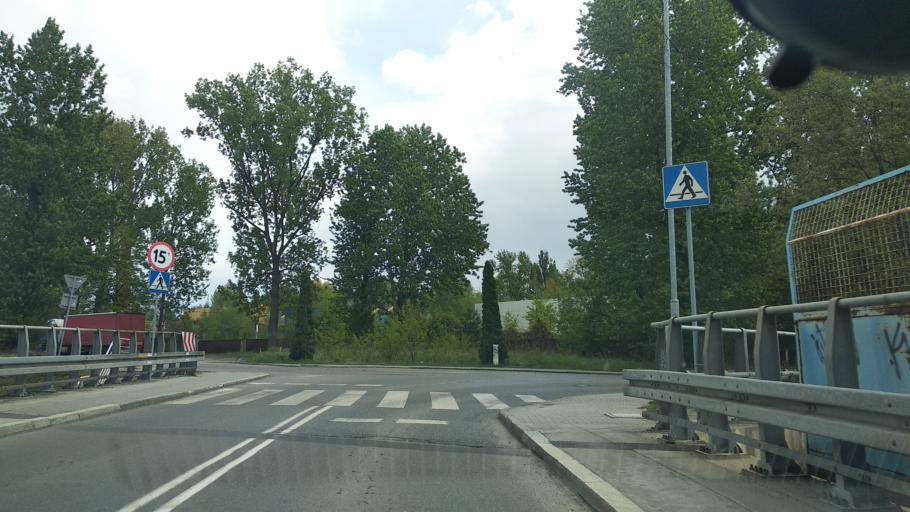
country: PL
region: Silesian Voivodeship
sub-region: Katowice
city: Katowice
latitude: 50.2437
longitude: 18.9827
